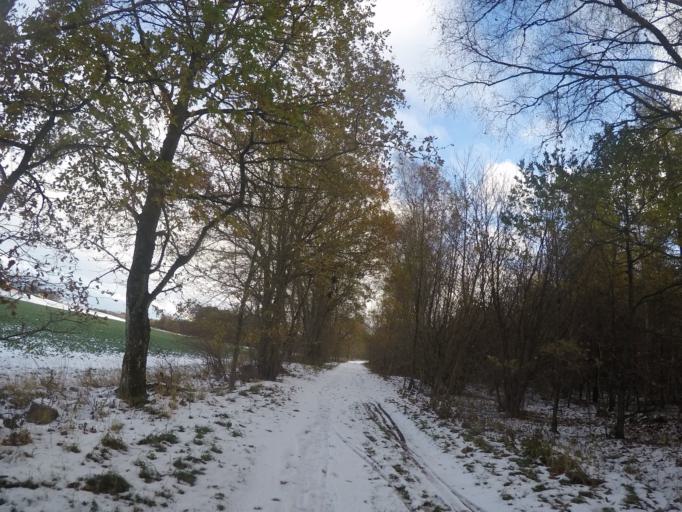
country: SE
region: Skane
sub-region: Lunds Kommun
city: Lund
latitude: 55.7858
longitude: 13.2208
